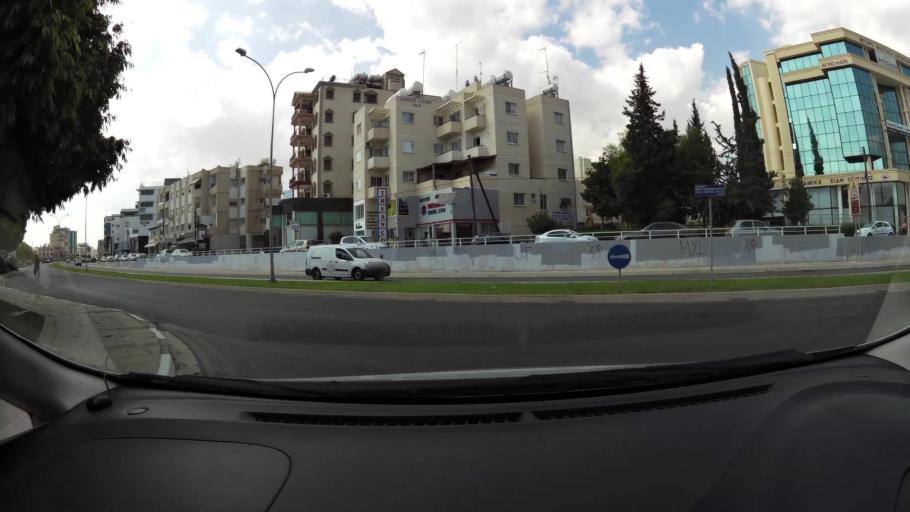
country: CY
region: Larnaka
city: Larnaca
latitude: 34.9185
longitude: 33.6140
